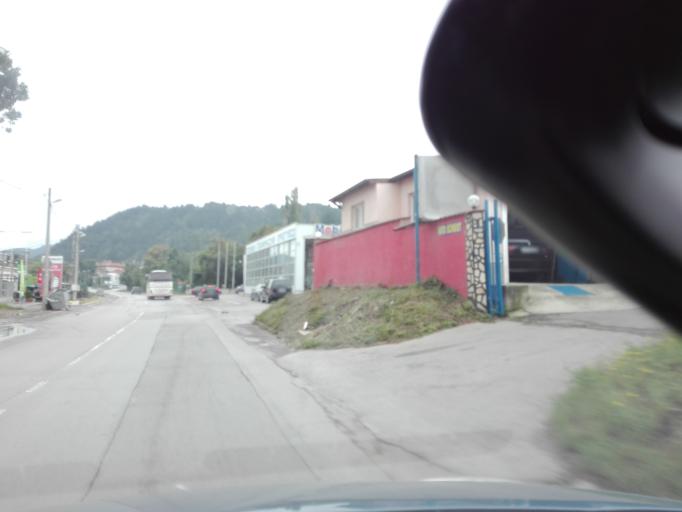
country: BG
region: Sofia-Capital
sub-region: Stolichna Obshtina
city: Sofia
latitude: 42.6106
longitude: 23.3993
